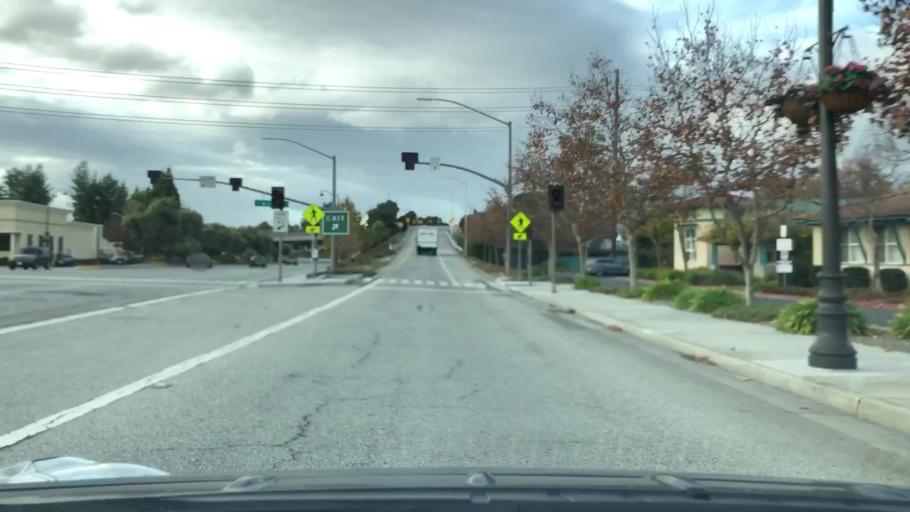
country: US
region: California
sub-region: Santa Clara County
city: Santa Clara
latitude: 37.3545
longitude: -121.9407
